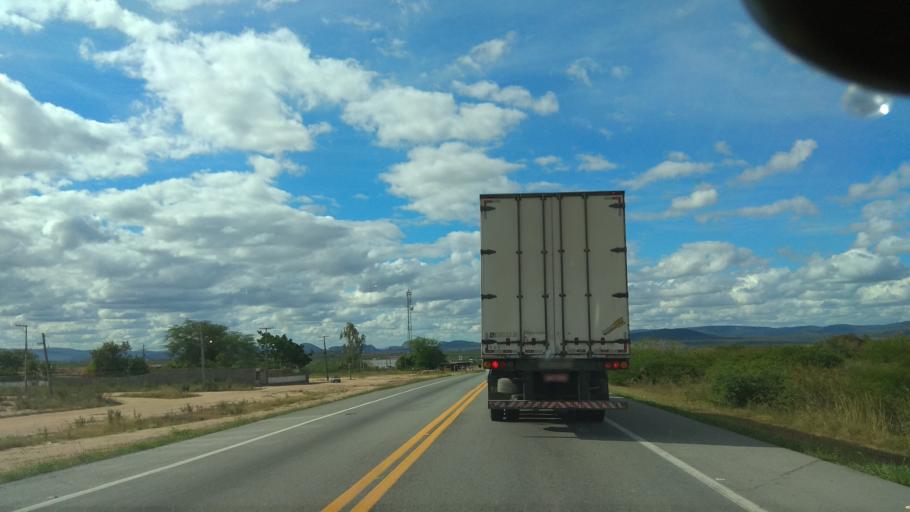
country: BR
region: Bahia
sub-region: Amargosa
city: Amargosa
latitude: -12.8583
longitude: -39.8494
